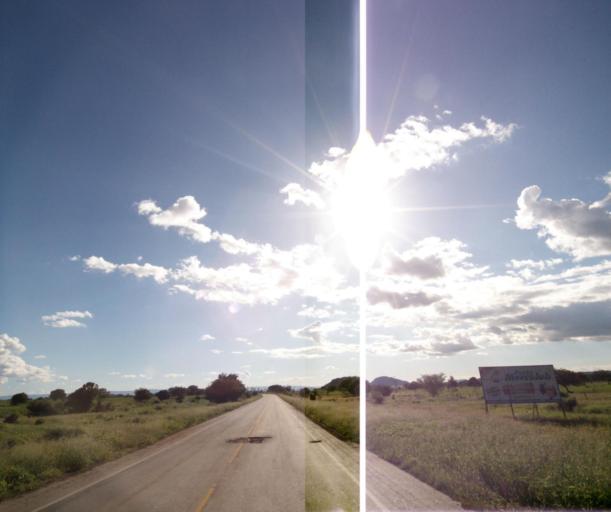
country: BR
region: Bahia
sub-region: Guanambi
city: Guanambi
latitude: -14.1611
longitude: -42.7148
